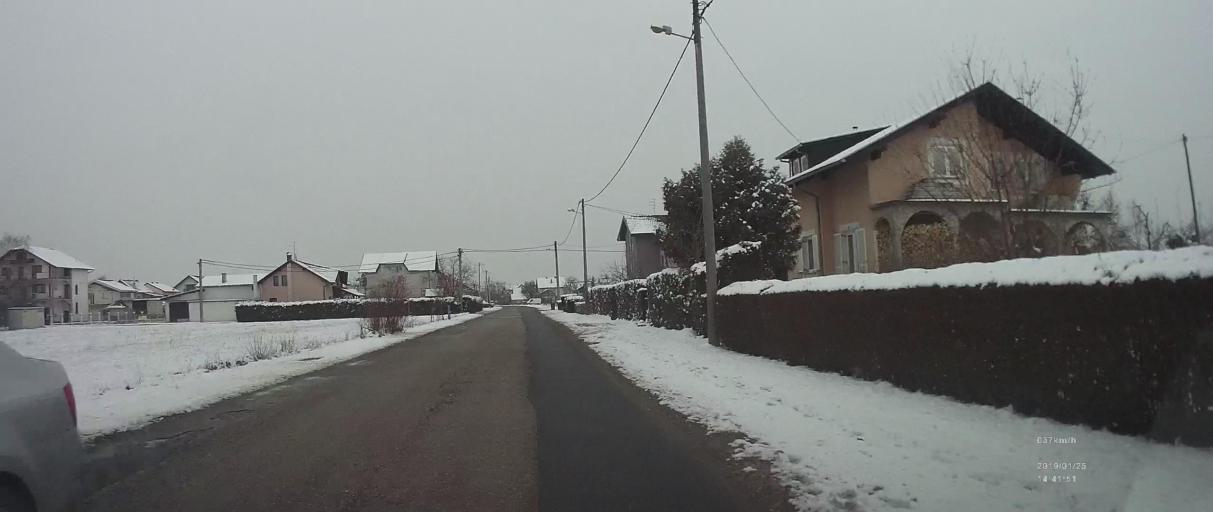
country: HR
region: Zagrebacka
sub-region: Grad Velika Gorica
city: Velika Gorica
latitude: 45.7056
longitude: 16.0715
